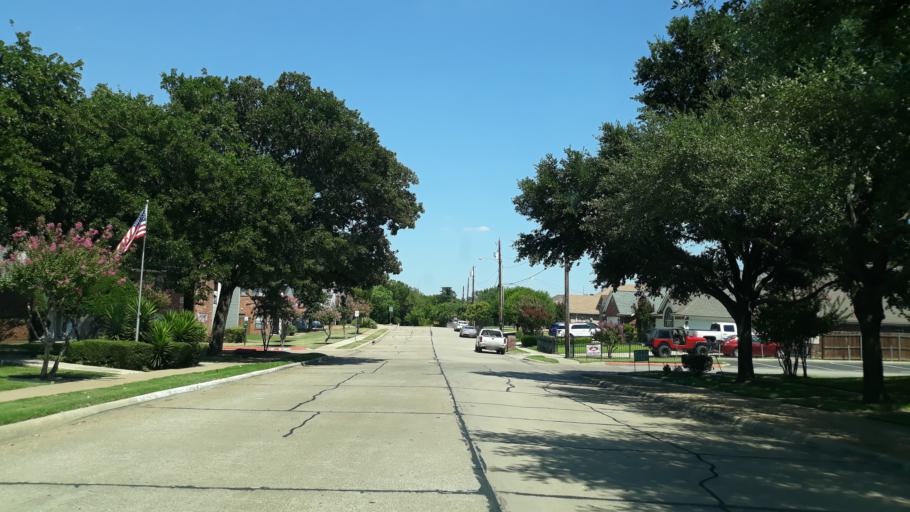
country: US
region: Texas
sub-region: Dallas County
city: Irving
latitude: 32.8266
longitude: -97.0011
